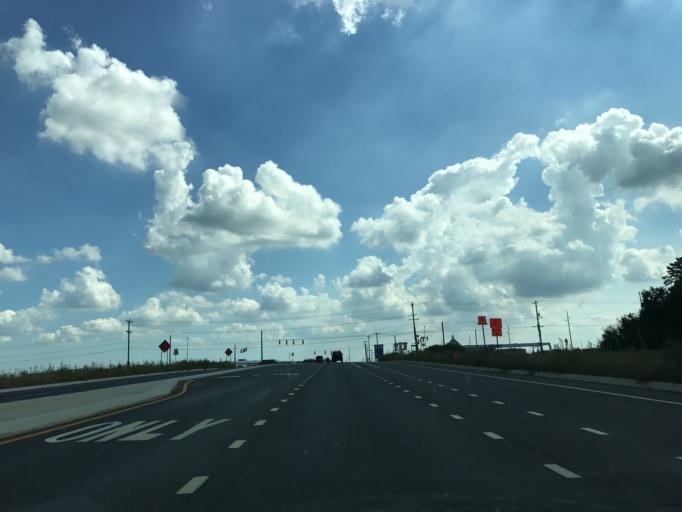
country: US
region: Delaware
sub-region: New Castle County
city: Middletown
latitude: 39.4418
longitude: -75.7478
